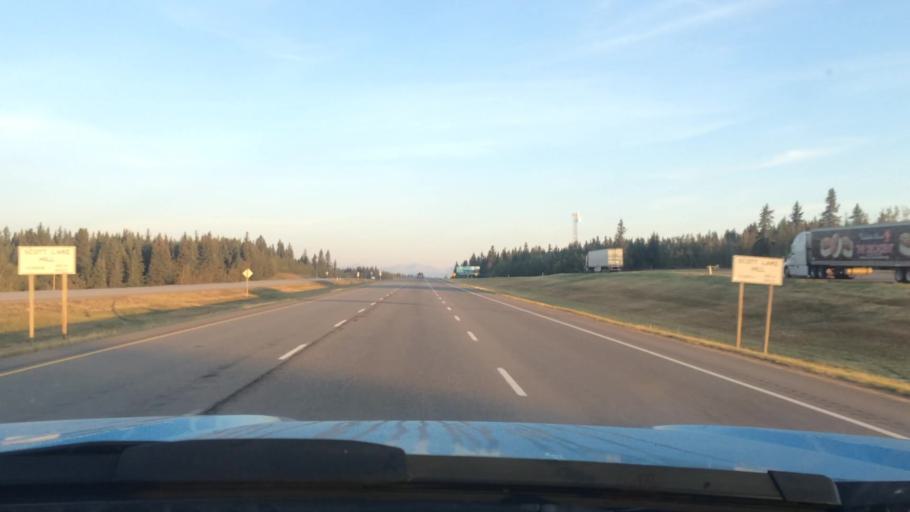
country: CA
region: Alberta
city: Cochrane
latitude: 51.1435
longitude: -114.7247
